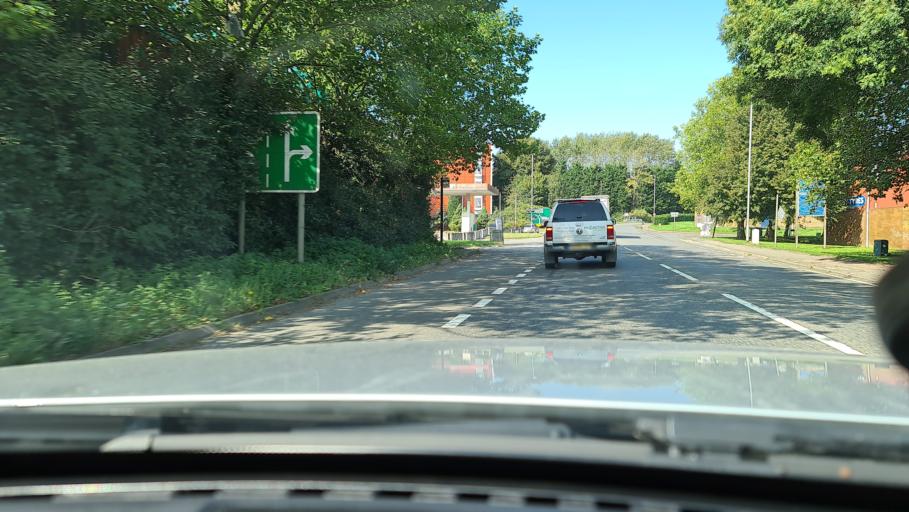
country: GB
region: England
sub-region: Northamptonshire
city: Daventry
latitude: 52.2462
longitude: -1.1485
